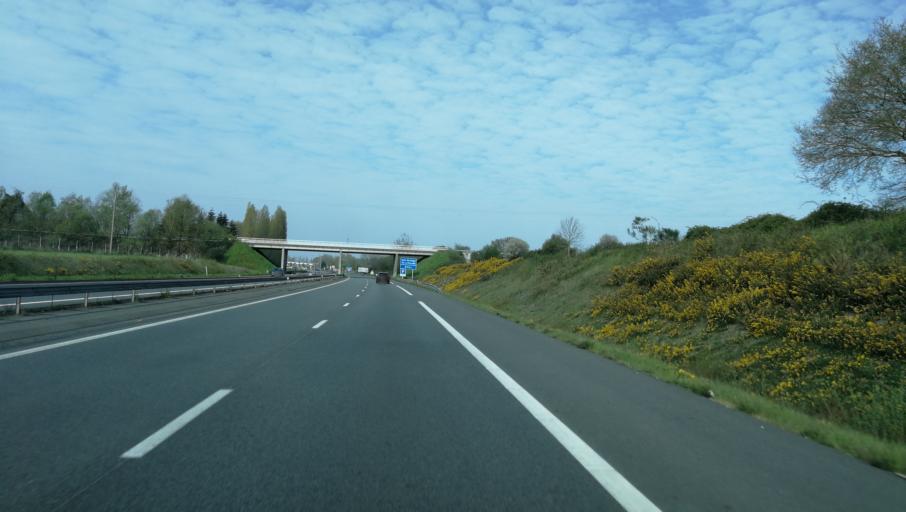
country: FR
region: Pays de la Loire
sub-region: Departement de la Mayenne
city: Saint-Pierre-la-Cour
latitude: 48.0824
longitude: -1.0148
